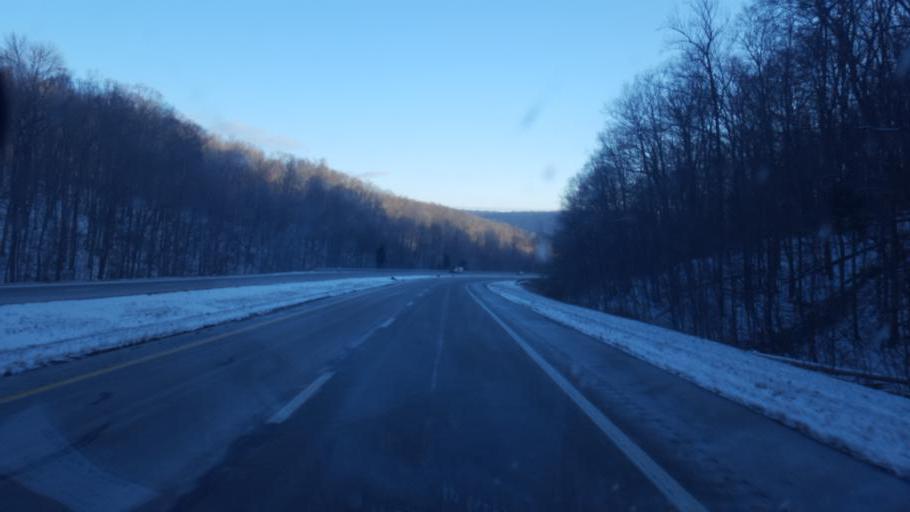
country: US
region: Ohio
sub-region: Adams County
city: Peebles
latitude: 39.0294
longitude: -83.2669
